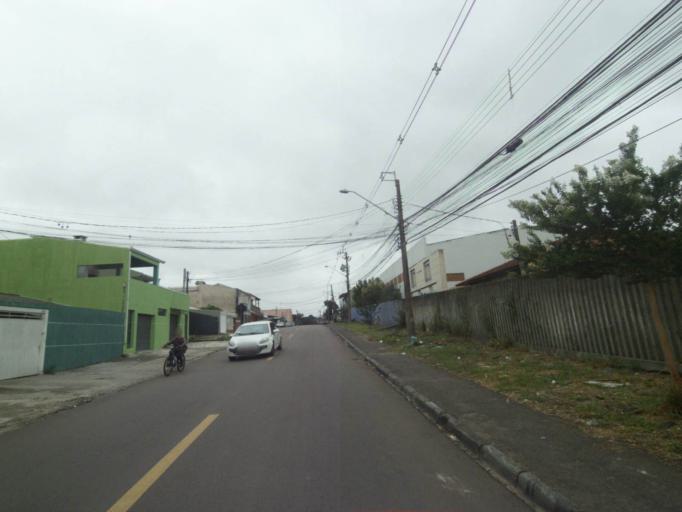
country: BR
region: Parana
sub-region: Curitiba
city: Curitiba
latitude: -25.4860
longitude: -49.3052
